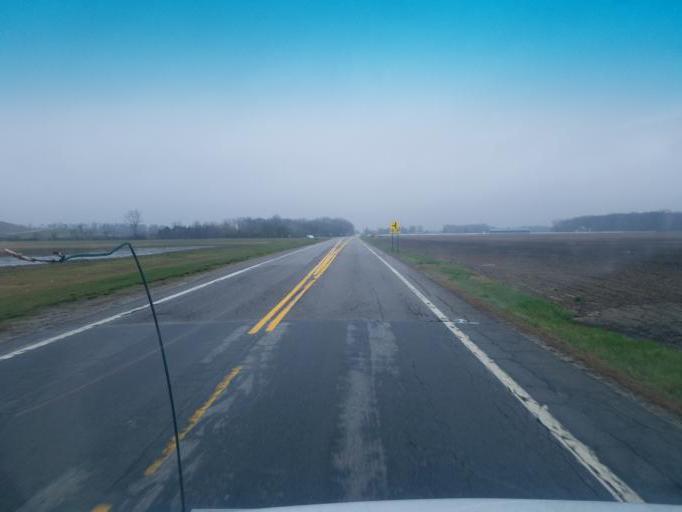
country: US
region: Ohio
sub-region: Wood County
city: Weston
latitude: 41.3722
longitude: -83.7414
